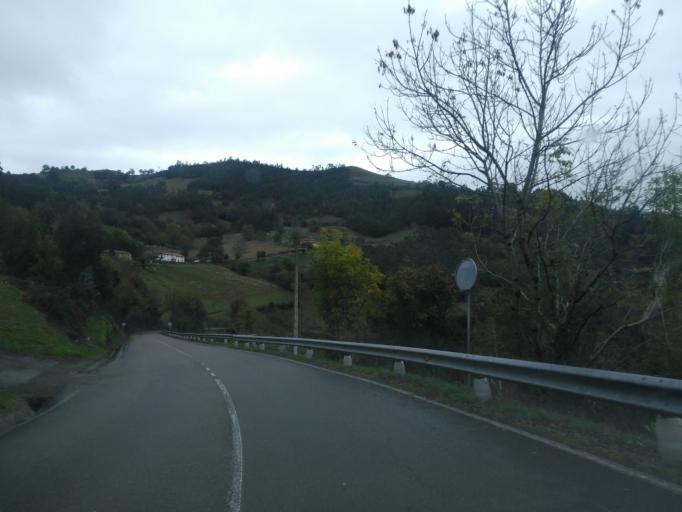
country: ES
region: Cantabria
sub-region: Provincia de Cantabria
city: Puente Viesgo
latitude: 43.2948
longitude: -3.9690
